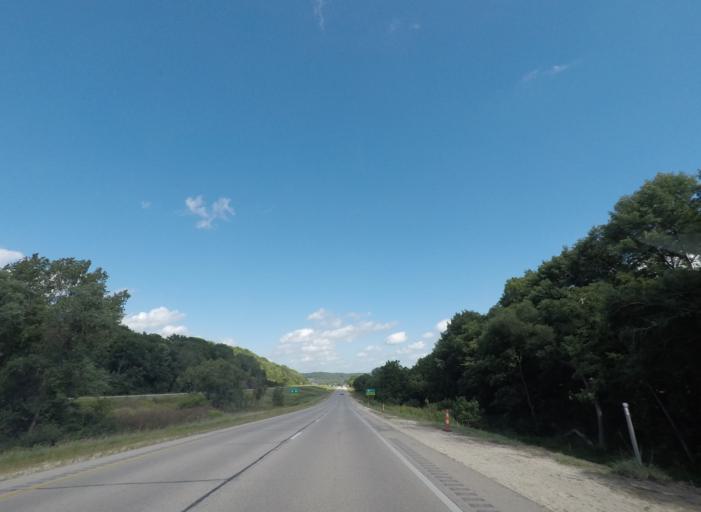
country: US
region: Iowa
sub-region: Dubuque County
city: Dubuque
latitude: 42.4179
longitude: -90.7131
